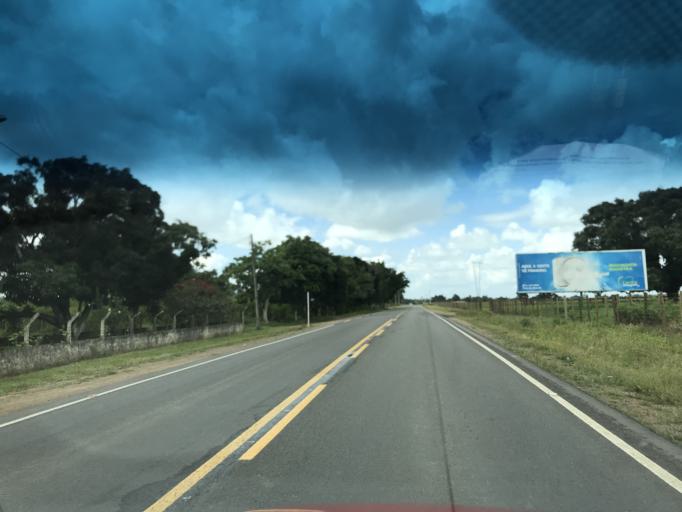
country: BR
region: Bahia
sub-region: Conceicao Do Almeida
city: Conceicao do Almeida
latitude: -12.7220
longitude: -39.2105
